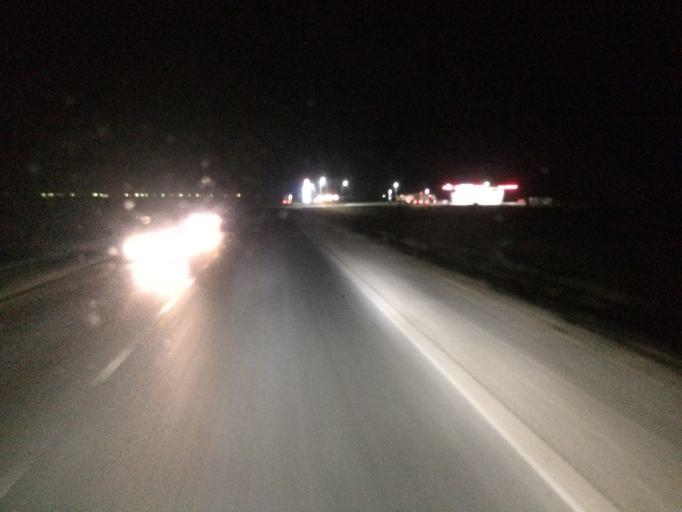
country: KZ
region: Batys Qazaqstan
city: Oral
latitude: 51.2170
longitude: 51.2768
